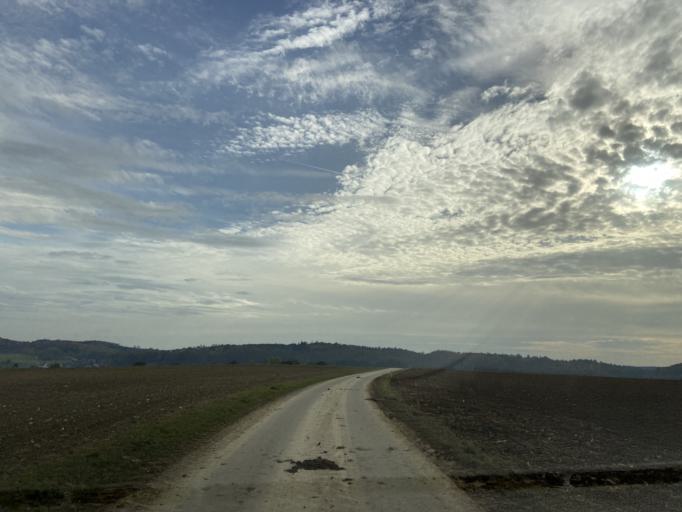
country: DE
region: Baden-Wuerttemberg
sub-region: Tuebingen Region
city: Bingen
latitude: 48.1027
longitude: 9.2720
